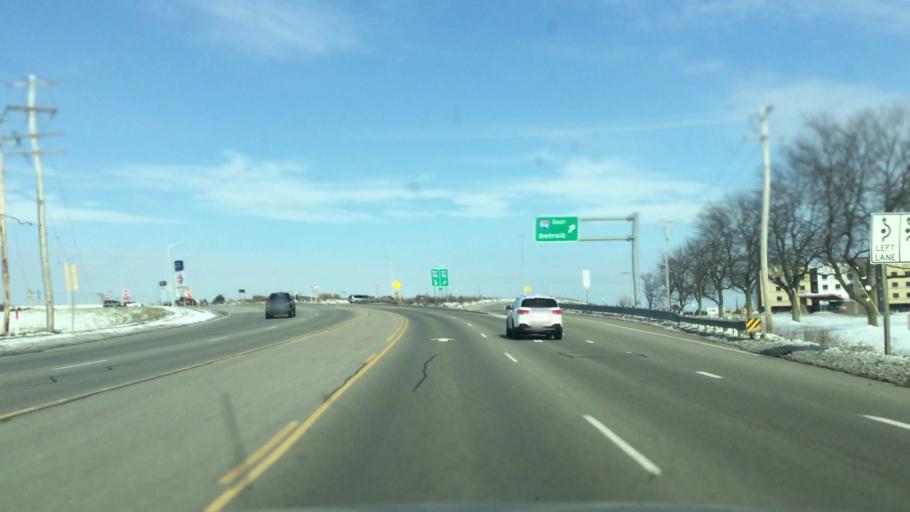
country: US
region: Michigan
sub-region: Kalamazoo County
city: Eastwood
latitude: 42.2562
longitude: -85.5308
